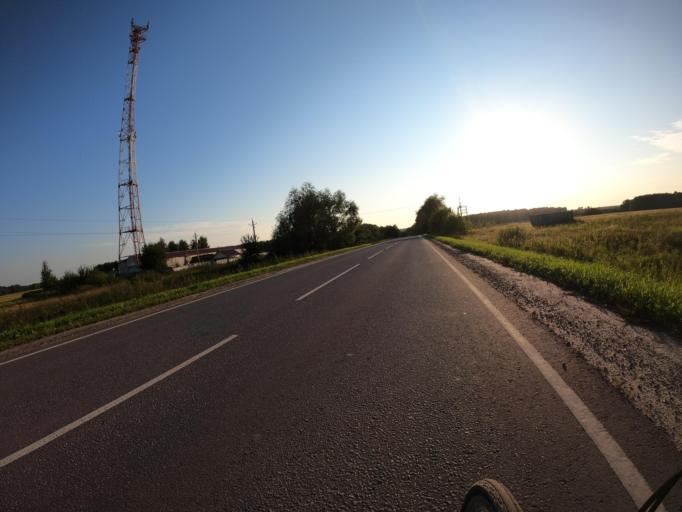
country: RU
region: Moskovskaya
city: Meshcherino
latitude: 55.1115
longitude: 38.3153
